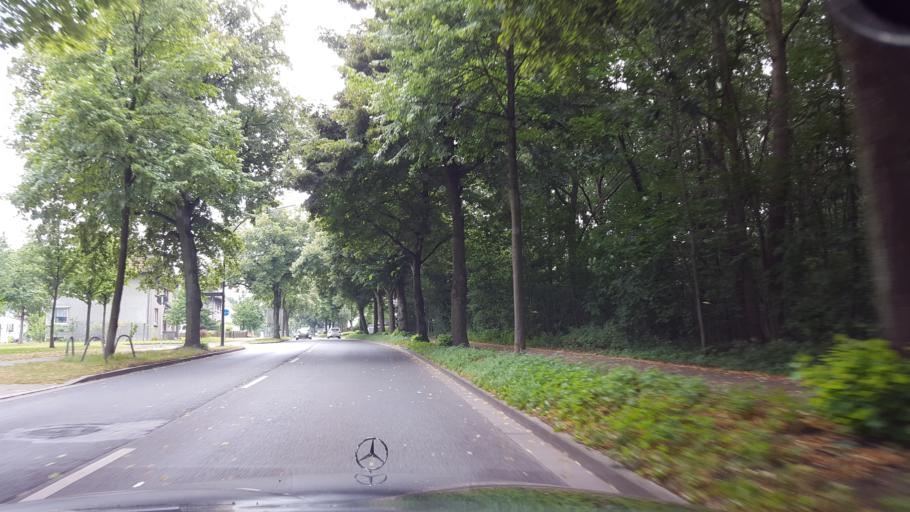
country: DE
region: North Rhine-Westphalia
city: Marl
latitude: 51.6850
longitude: 7.1168
